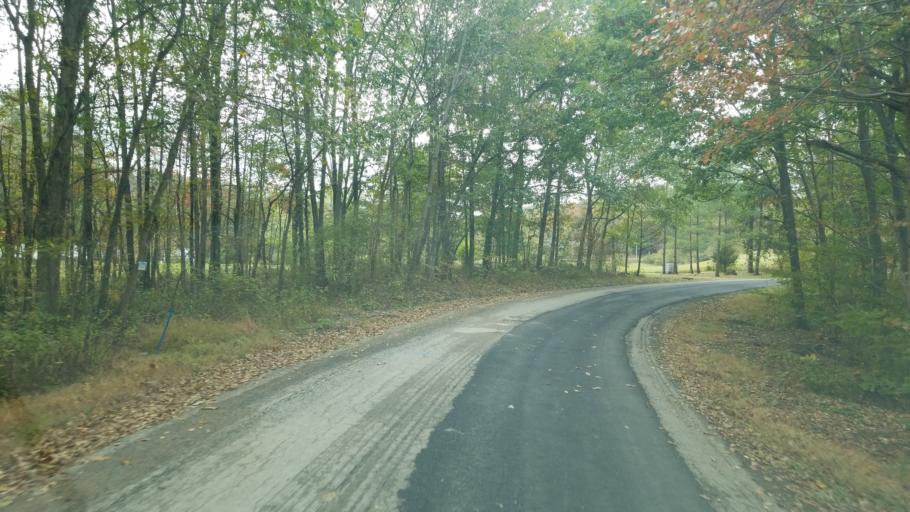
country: US
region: Ohio
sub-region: Jackson County
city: Wellston
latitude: 39.1560
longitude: -82.5949
